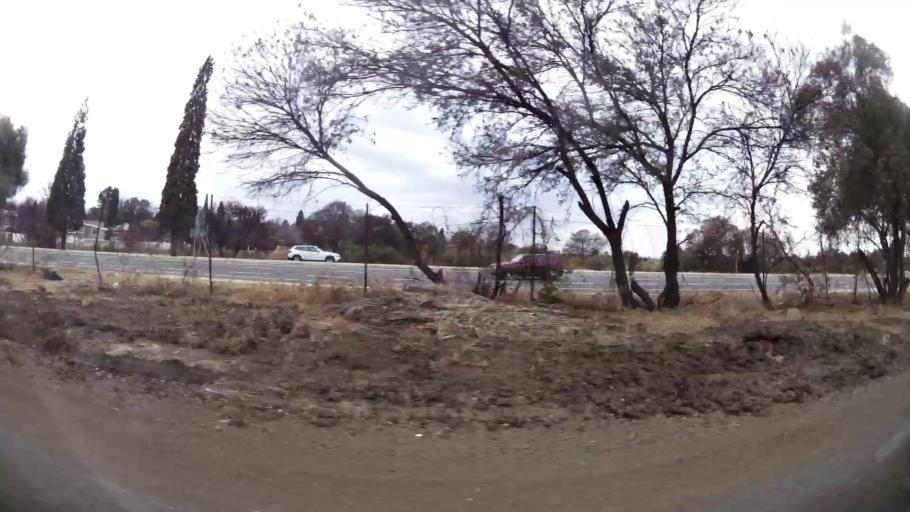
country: ZA
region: Orange Free State
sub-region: Fezile Dabi District Municipality
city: Kroonstad
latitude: -27.6830
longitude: 27.2405
